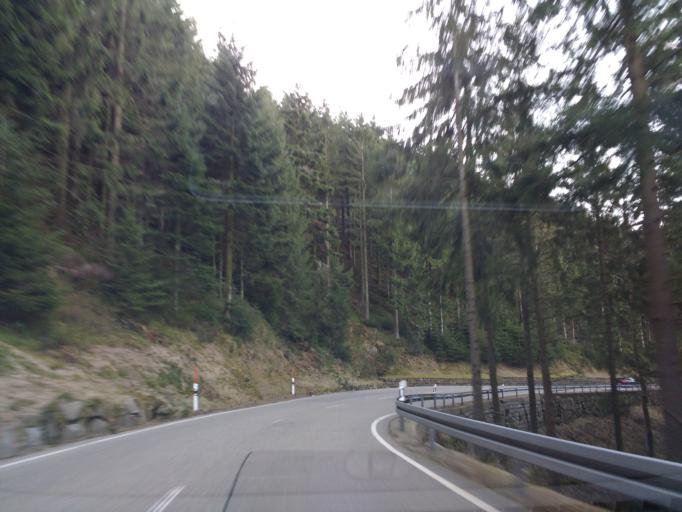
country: DE
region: Baden-Wuerttemberg
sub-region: Freiburg Region
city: Bad Peterstal-Griesbach
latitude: 48.4595
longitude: 8.2612
